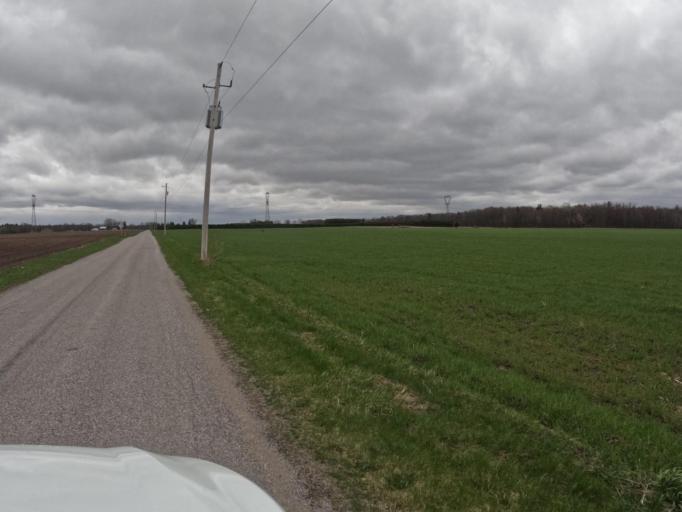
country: CA
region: Ontario
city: Norfolk County
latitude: 42.9537
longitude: -80.4243
